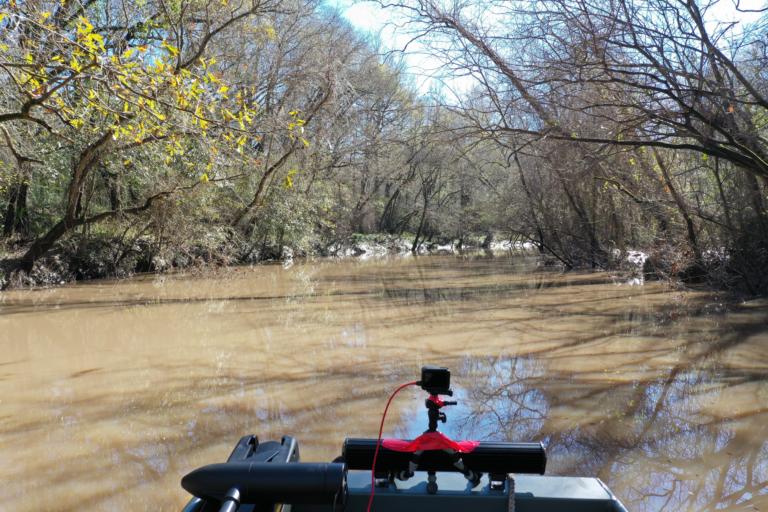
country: US
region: Louisiana
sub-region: Calcasieu Parish
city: Iowa
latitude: 30.3172
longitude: -93.0494
